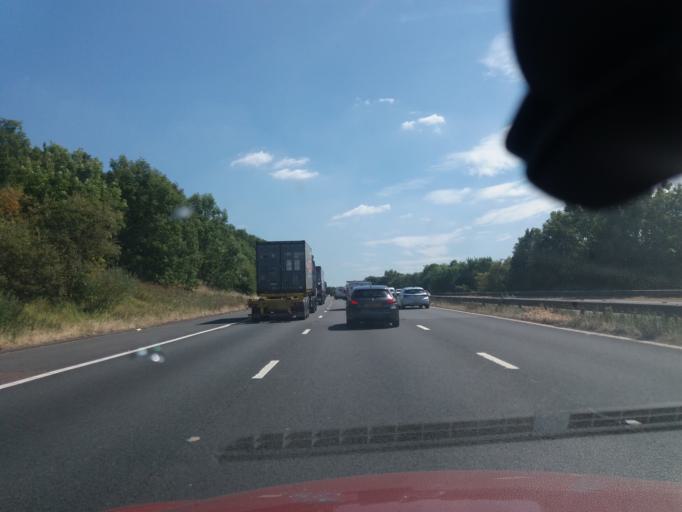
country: GB
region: England
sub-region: Lancashire
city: Chorley
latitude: 53.6512
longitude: -2.6086
